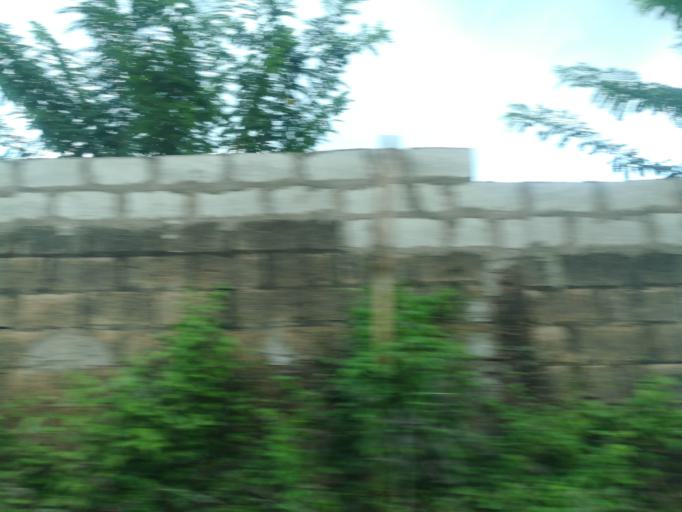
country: NG
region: Oyo
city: Ibadan
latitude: 7.4338
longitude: 3.9054
